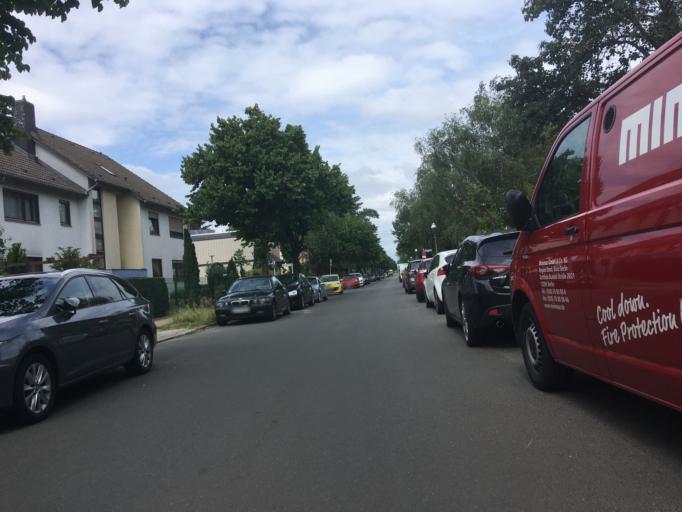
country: DE
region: Berlin
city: Lichtenrade
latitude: 52.4070
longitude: 13.3909
